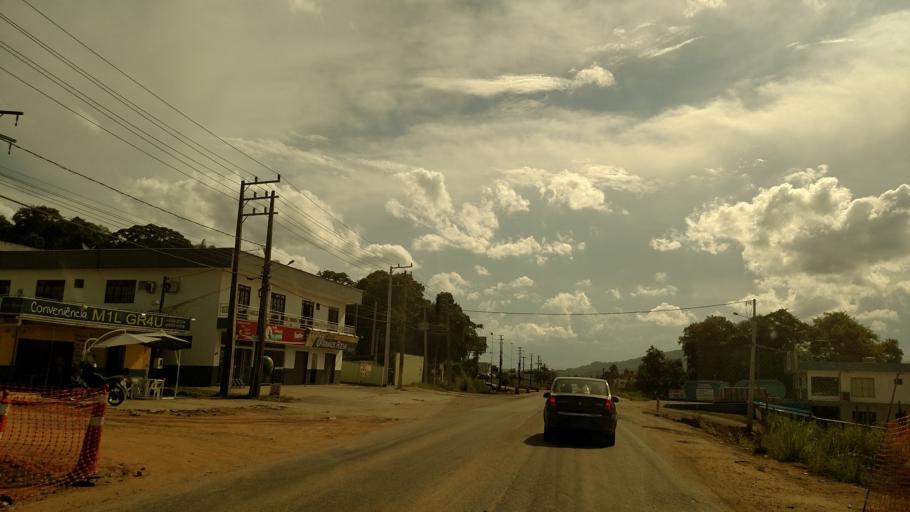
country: BR
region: Santa Catarina
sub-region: Itajai
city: Itajai
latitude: -26.9467
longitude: -48.7379
